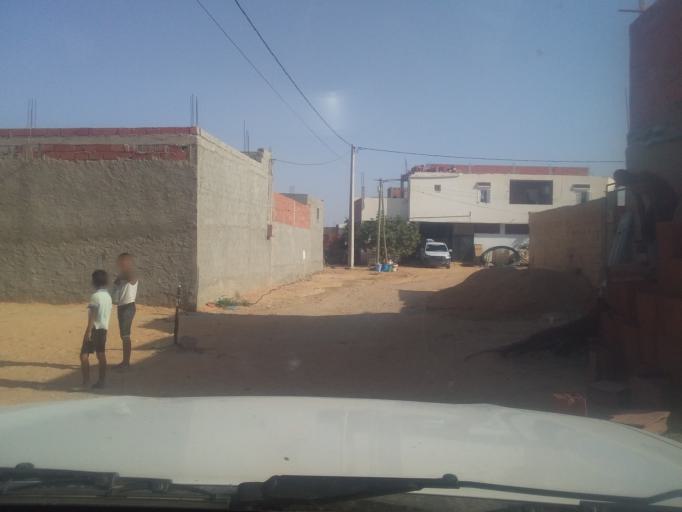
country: TN
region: Qabis
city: Matmata
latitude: 33.6093
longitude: 10.2793
